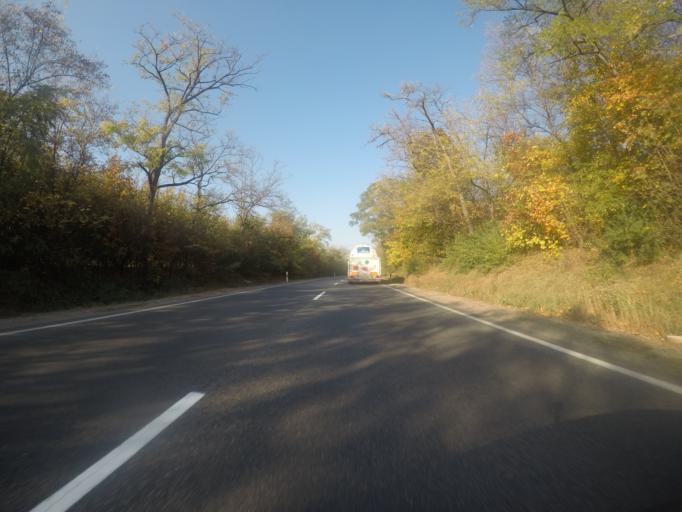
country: HU
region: Fejer
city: dunaujvaros
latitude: 46.9682
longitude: 18.9073
